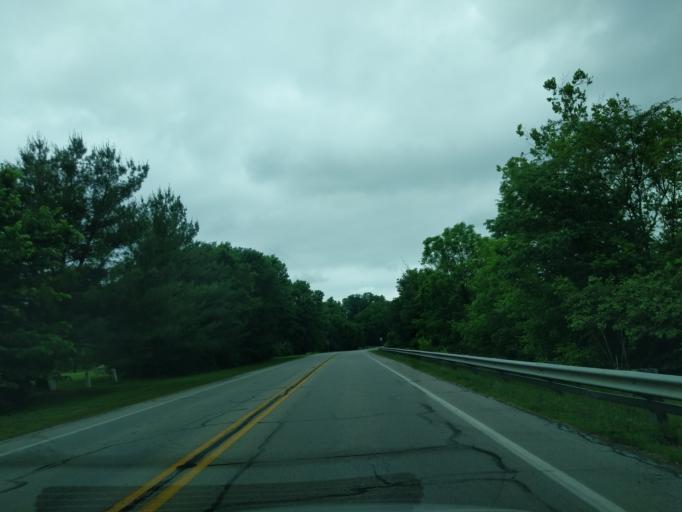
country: US
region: Indiana
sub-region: Hamilton County
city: Noblesville
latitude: 40.0549
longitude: -86.0158
